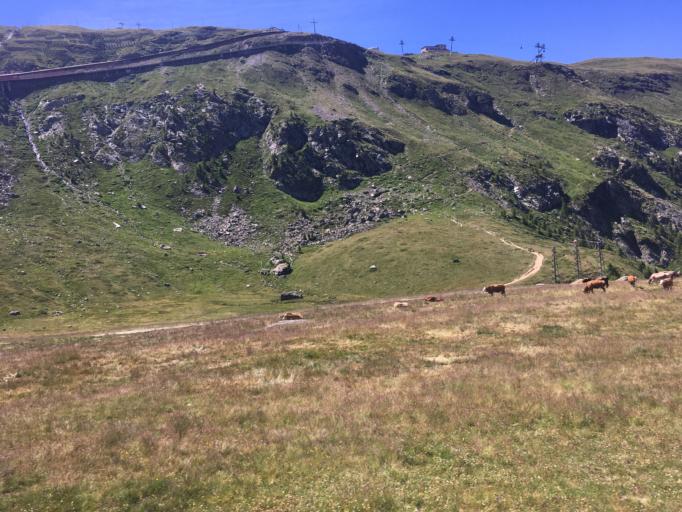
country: CH
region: Valais
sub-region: Visp District
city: Zermatt
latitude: 46.0011
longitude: 7.7555
